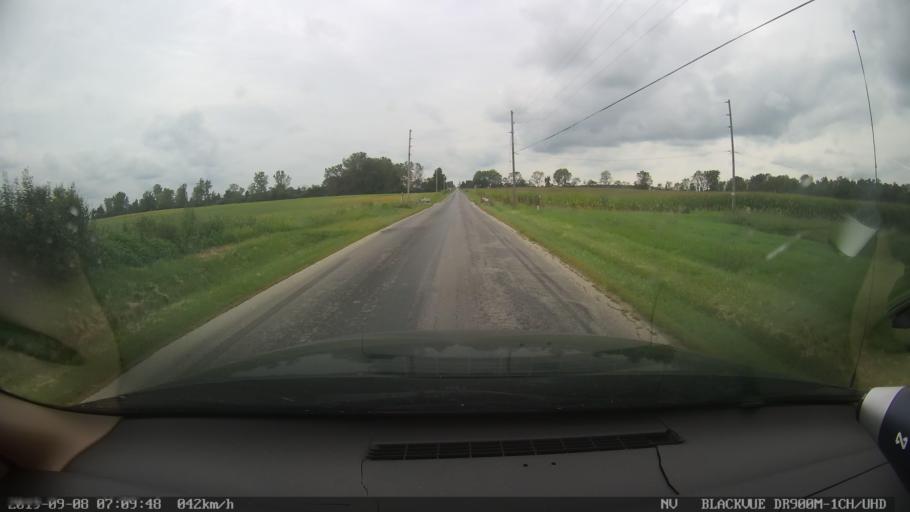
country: US
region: Ohio
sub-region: Richland County
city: Shelby
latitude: 40.9085
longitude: -82.6720
